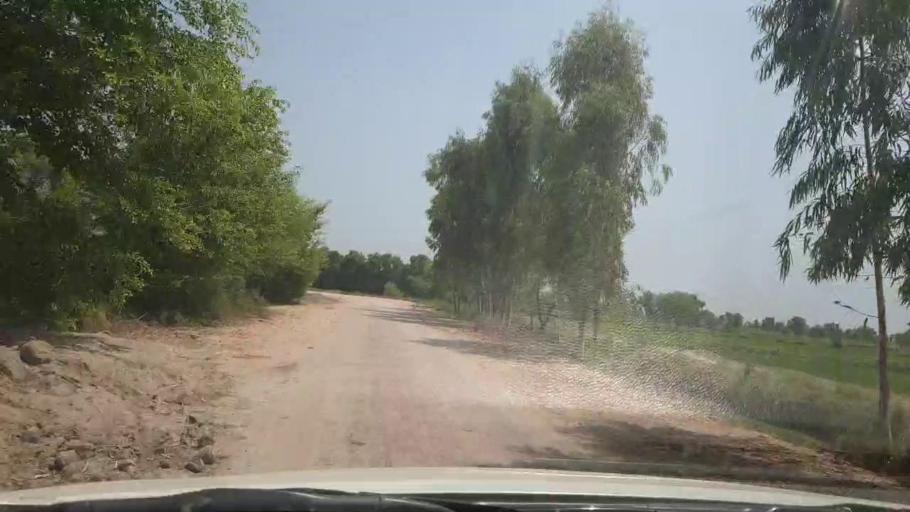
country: PK
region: Sindh
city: Rustam jo Goth
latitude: 28.0277
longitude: 68.7600
